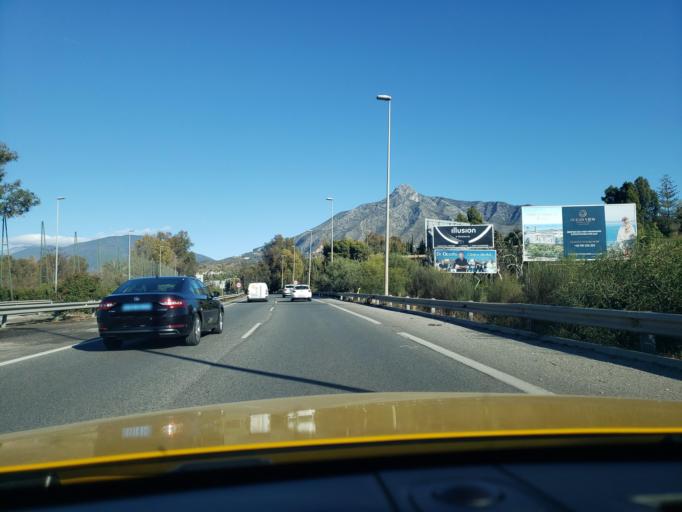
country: ES
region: Andalusia
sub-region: Provincia de Malaga
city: Marbella
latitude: 36.4994
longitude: -4.9472
